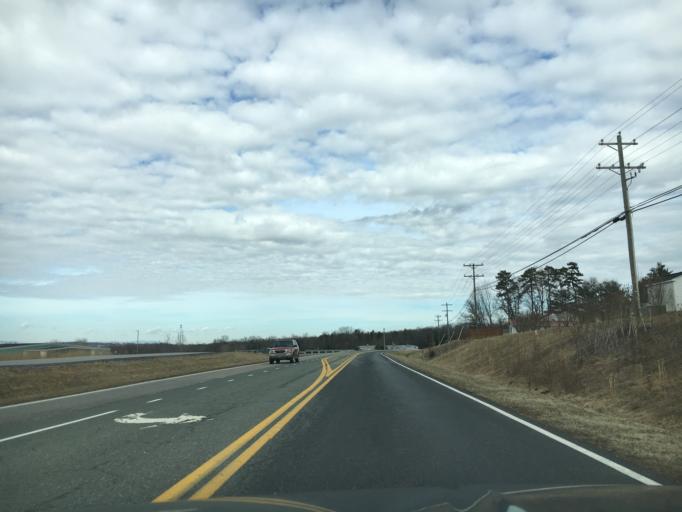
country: US
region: Virginia
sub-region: Augusta County
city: Crimora
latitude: 38.1368
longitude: -78.8452
